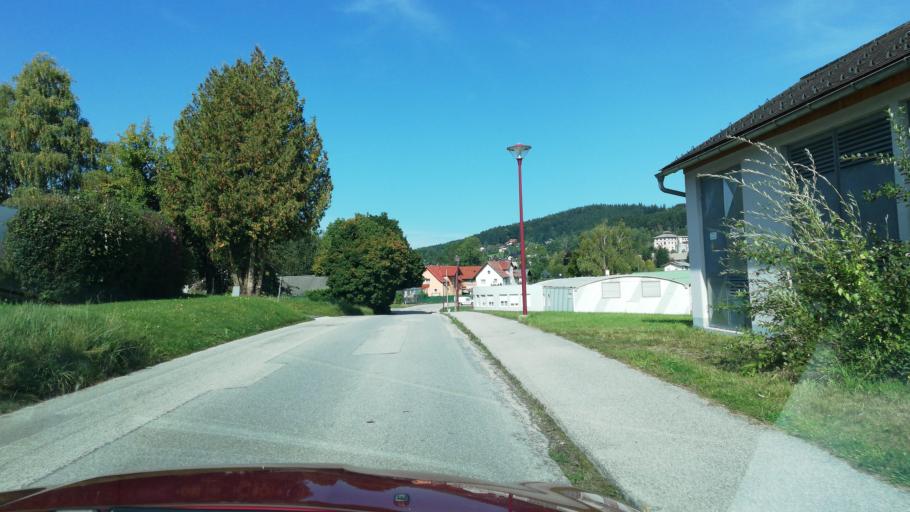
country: AT
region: Upper Austria
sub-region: Politischer Bezirk Vocklabruck
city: Redleiten
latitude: 48.0889
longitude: 13.5602
